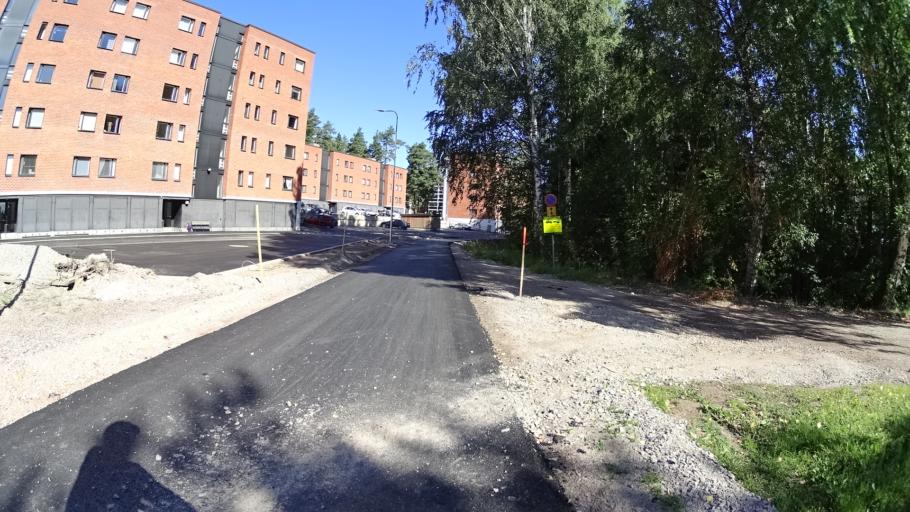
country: FI
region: Uusimaa
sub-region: Helsinki
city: Kerava
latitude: 60.4114
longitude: 25.1067
